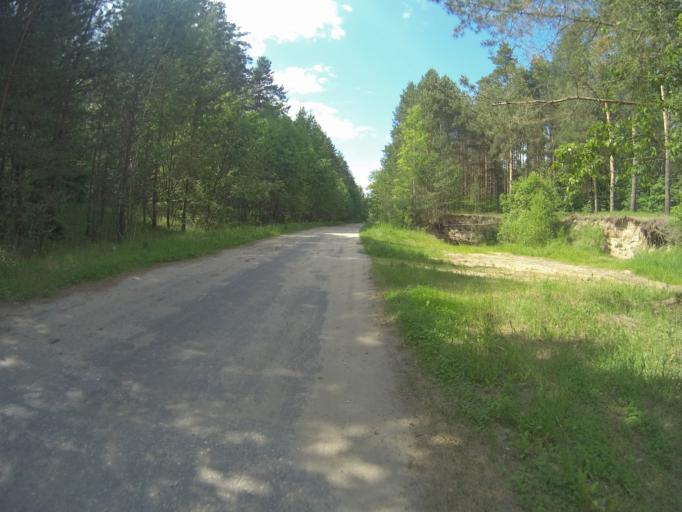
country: RU
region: Vladimir
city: Vorsha
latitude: 56.0081
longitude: 40.1974
